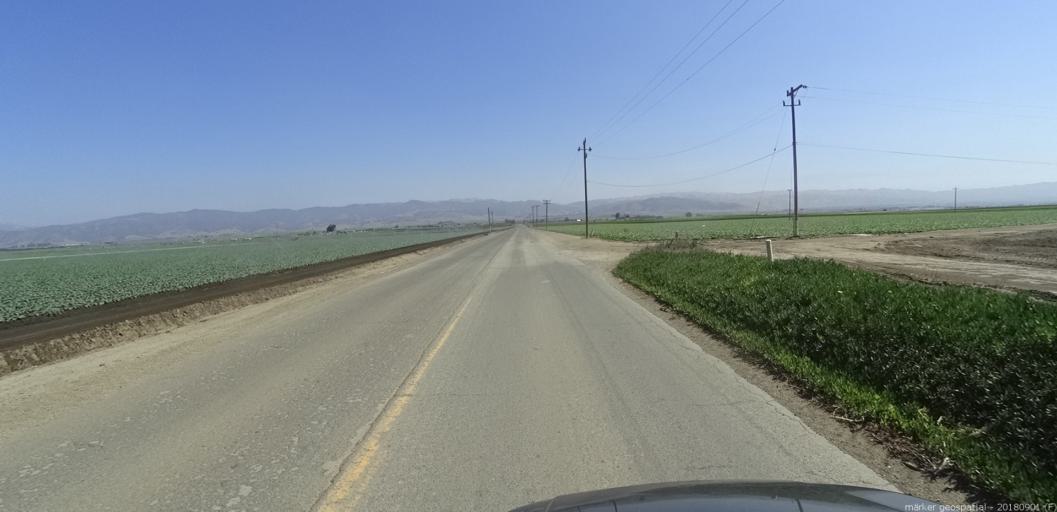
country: US
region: California
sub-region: Monterey County
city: Chualar
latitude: 36.5531
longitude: -121.5381
